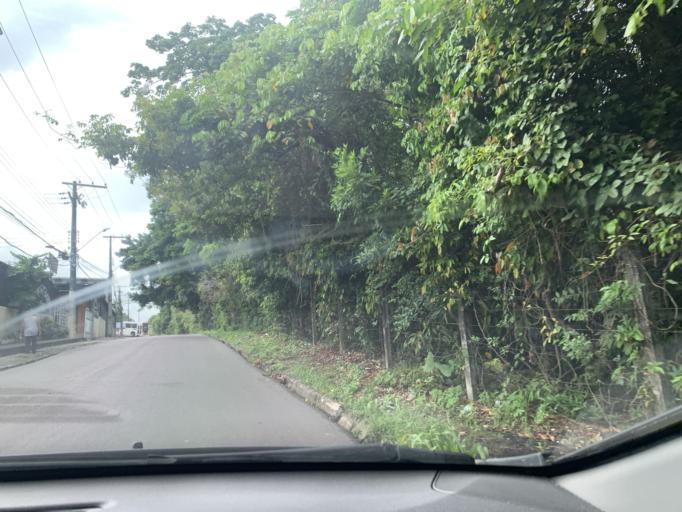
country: BR
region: Amazonas
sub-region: Manaus
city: Manaus
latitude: -3.0871
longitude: -59.9749
